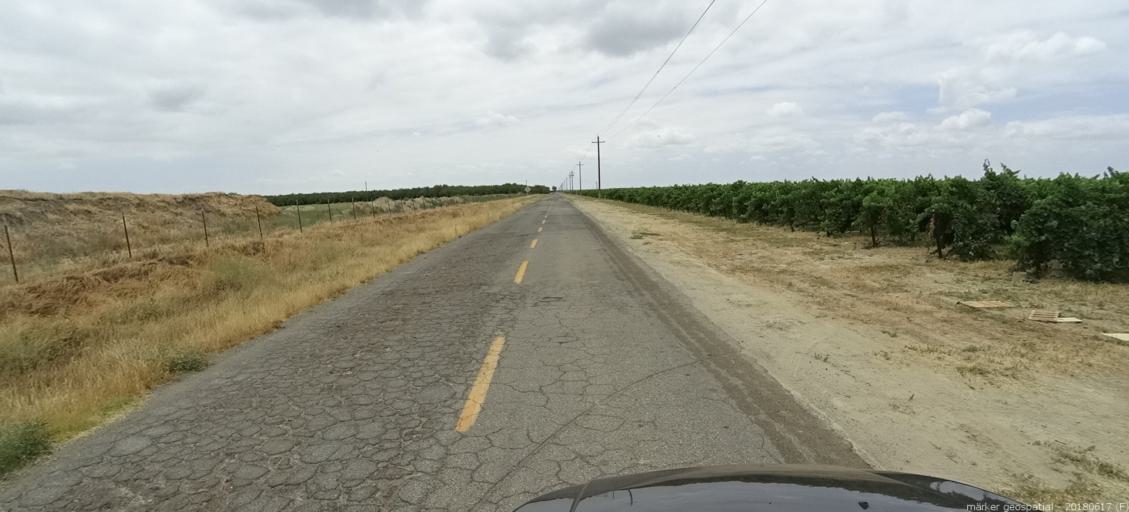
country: US
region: California
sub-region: Madera County
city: Parkwood
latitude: 36.8504
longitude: -120.1647
